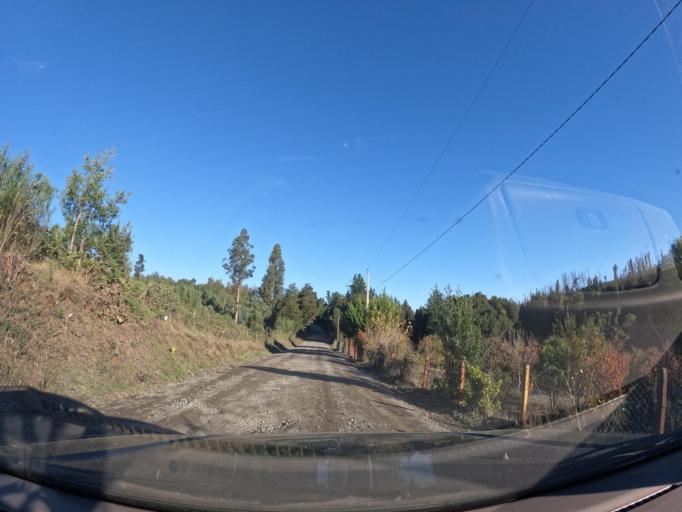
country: CL
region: Biobio
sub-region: Provincia de Concepcion
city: Chiguayante
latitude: -37.0177
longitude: -72.8922
